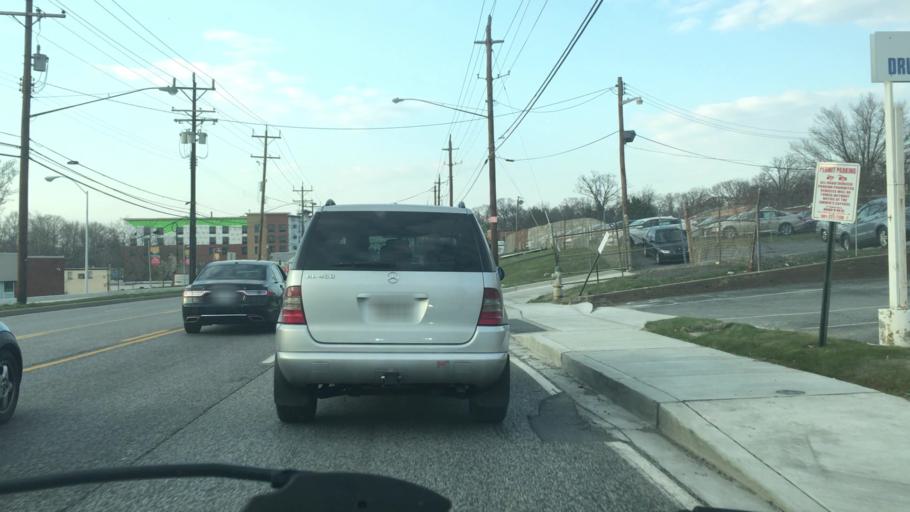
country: US
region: Maryland
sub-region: Prince George's County
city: Berwyn Heights
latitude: 39.0096
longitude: -76.9289
